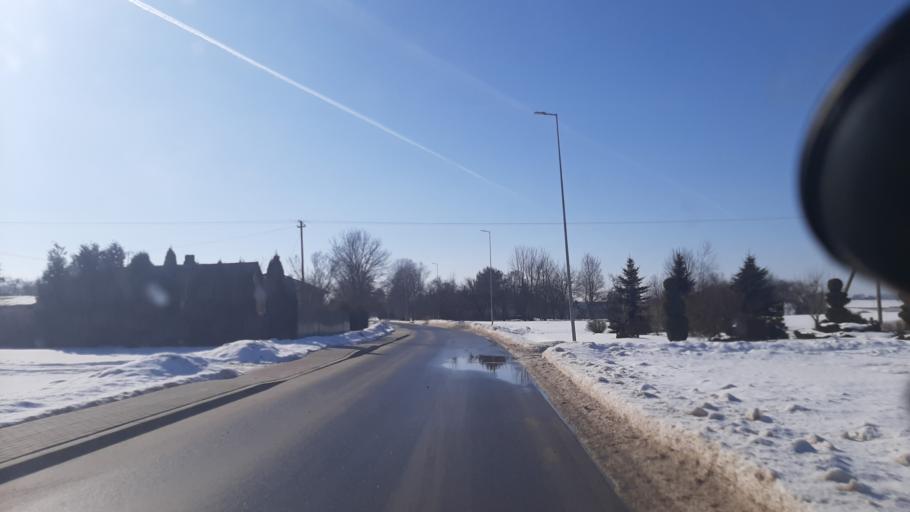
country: PL
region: Lublin Voivodeship
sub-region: Powiat lubelski
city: Garbow
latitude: 51.3033
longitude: 22.3073
